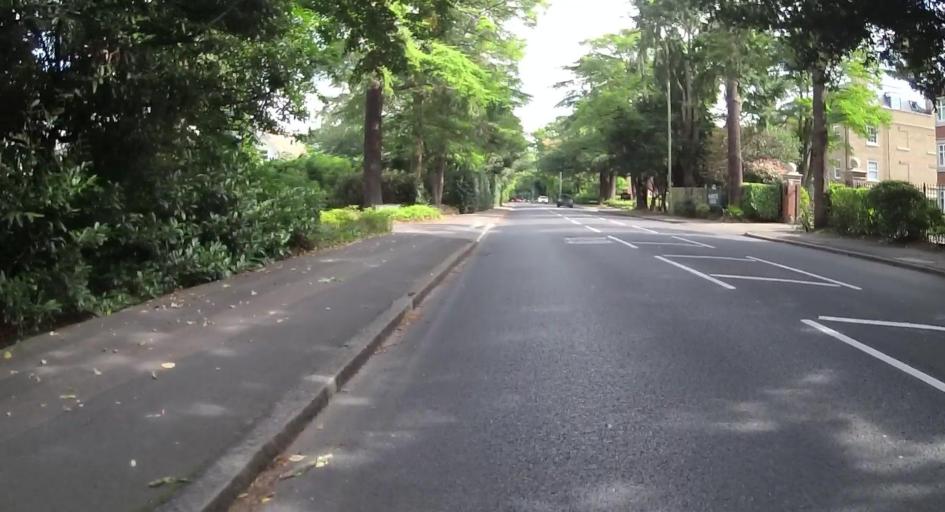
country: GB
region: England
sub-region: Surrey
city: Weybridge
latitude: 51.3656
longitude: -0.4390
